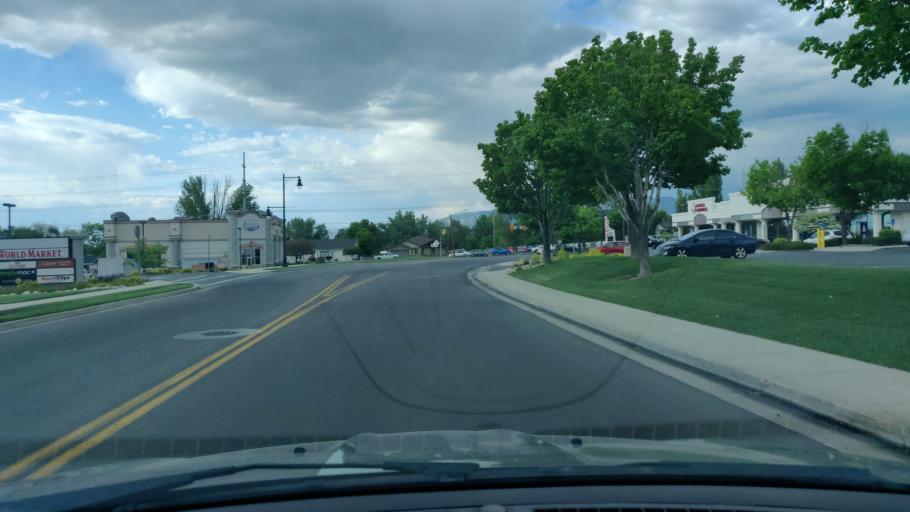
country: US
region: Utah
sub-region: Salt Lake County
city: Little Cottonwood Creek Valley
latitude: 40.6244
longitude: -111.8513
